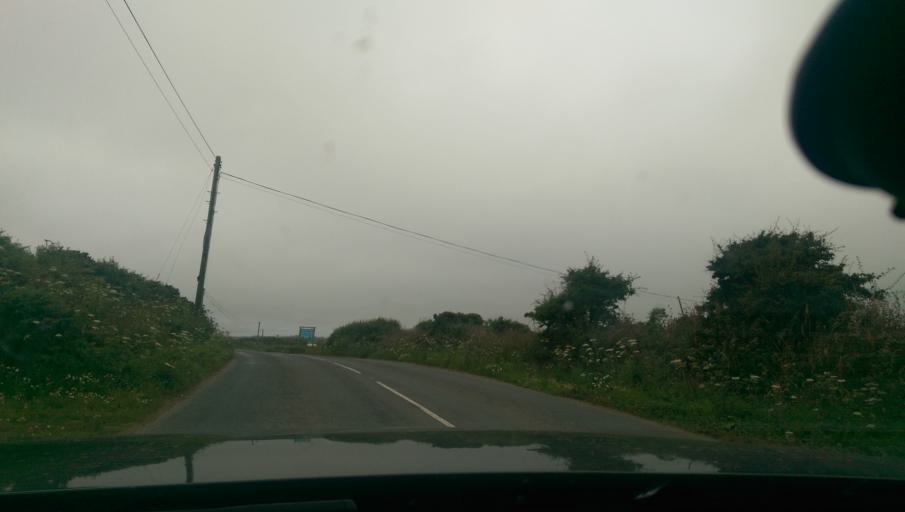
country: GB
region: England
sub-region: Cornwall
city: St. Buryan
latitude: 50.0910
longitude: -5.6337
